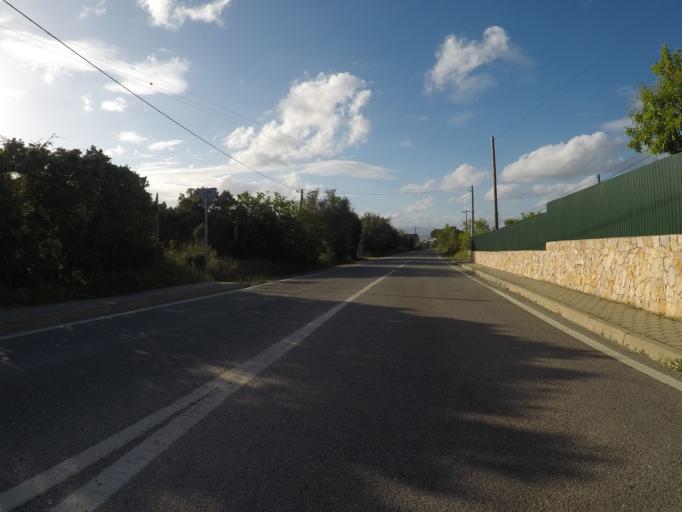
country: PT
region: Faro
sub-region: Lagoa
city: Carvoeiro
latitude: 37.1018
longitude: -8.4440
